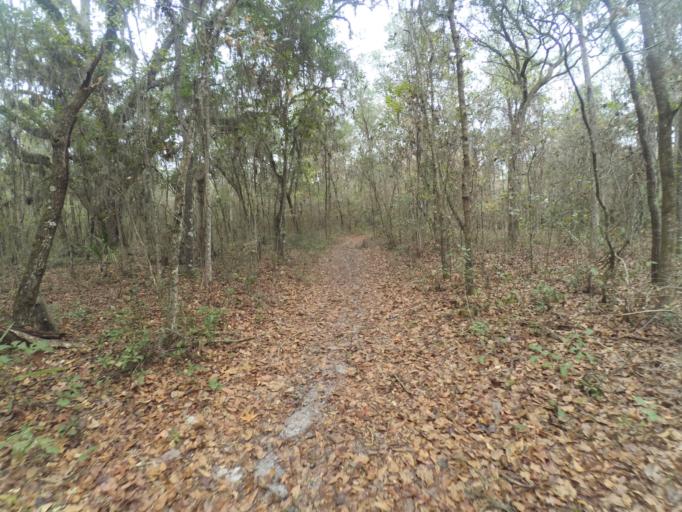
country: US
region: Florida
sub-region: Alachua County
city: Gainesville
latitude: 29.5443
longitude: -82.2730
